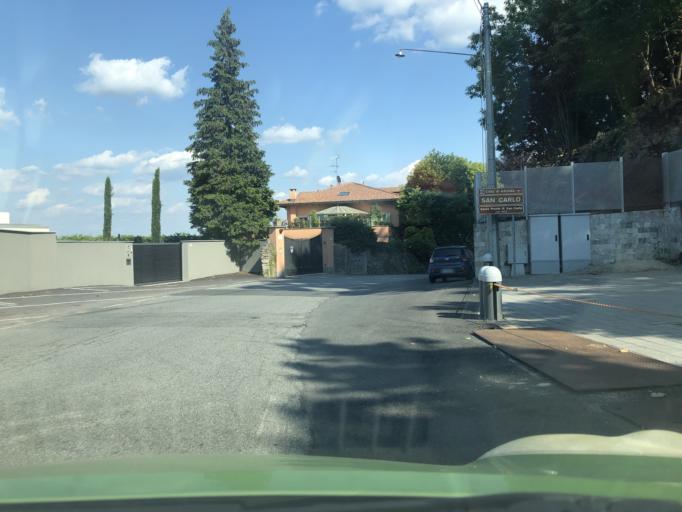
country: IT
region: Piedmont
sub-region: Provincia di Novara
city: Arona
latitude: 45.7718
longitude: 8.5421
